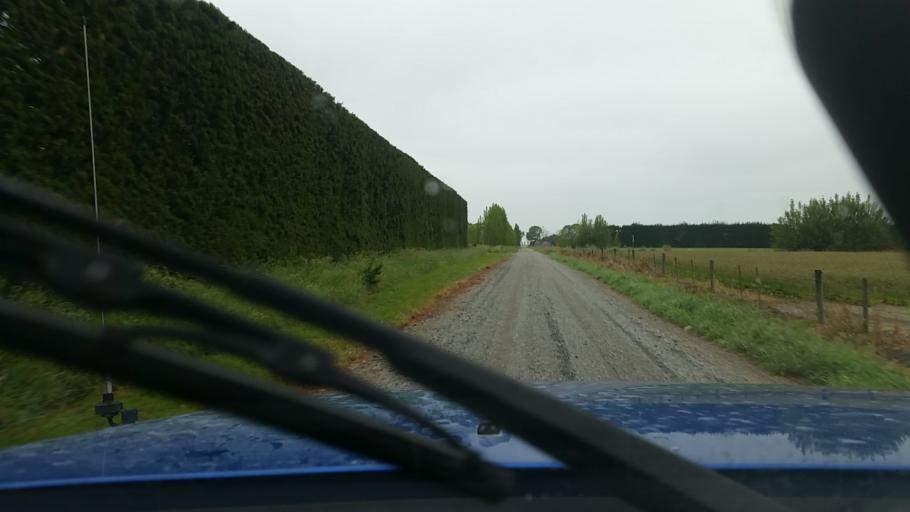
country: NZ
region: Canterbury
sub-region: Ashburton District
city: Tinwald
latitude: -44.0235
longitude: 171.7205
